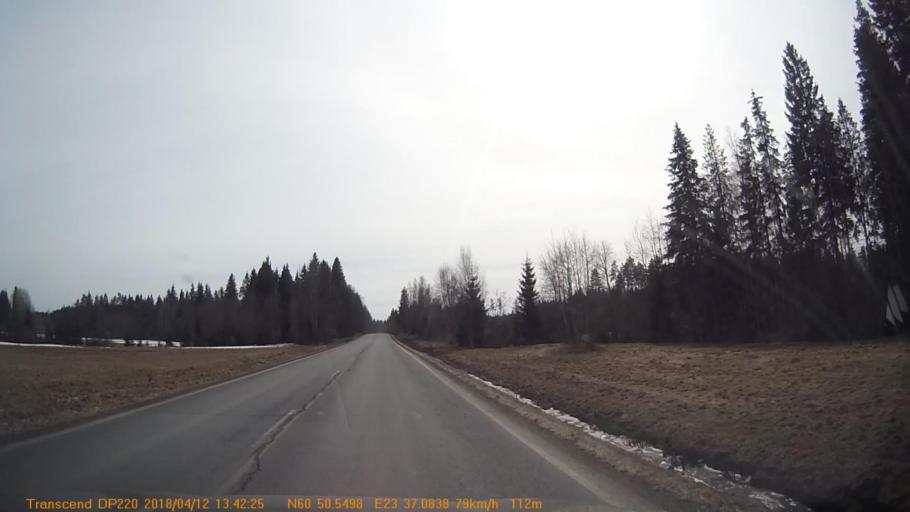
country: FI
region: Haeme
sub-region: Forssa
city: Forssa
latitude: 60.8418
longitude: 23.6181
